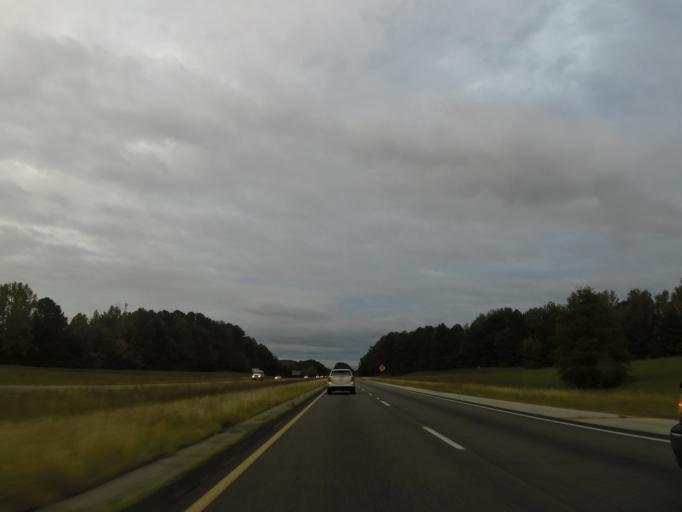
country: US
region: Alabama
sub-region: Saint Clair County
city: Springville
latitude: 33.7772
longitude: -86.4268
